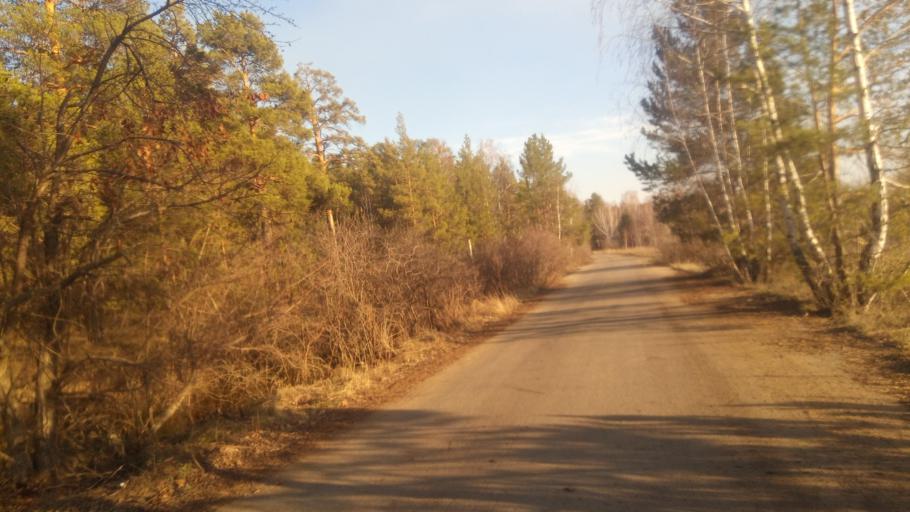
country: RU
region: Chelyabinsk
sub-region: Gorod Chelyabinsk
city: Chelyabinsk
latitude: 55.1358
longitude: 61.3272
